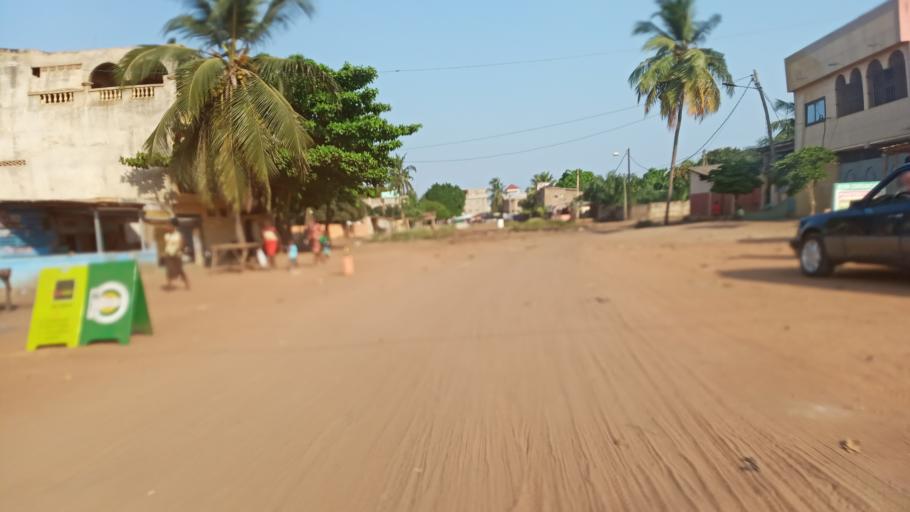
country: TG
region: Maritime
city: Lome
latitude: 6.1805
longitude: 1.1606
